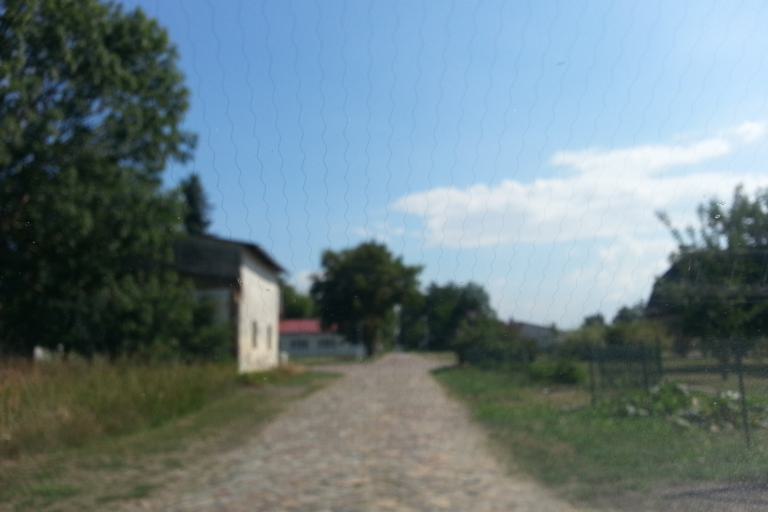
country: DE
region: Mecklenburg-Vorpommern
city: Ferdinandshof
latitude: 53.7020
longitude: 13.8324
